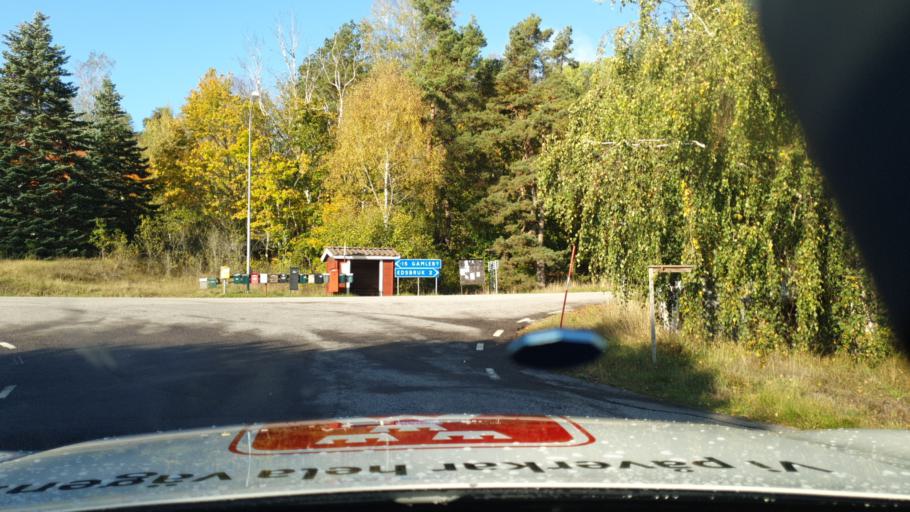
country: SE
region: Kalmar
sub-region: Vasterviks Kommun
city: Forserum
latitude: 58.0006
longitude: 16.5043
